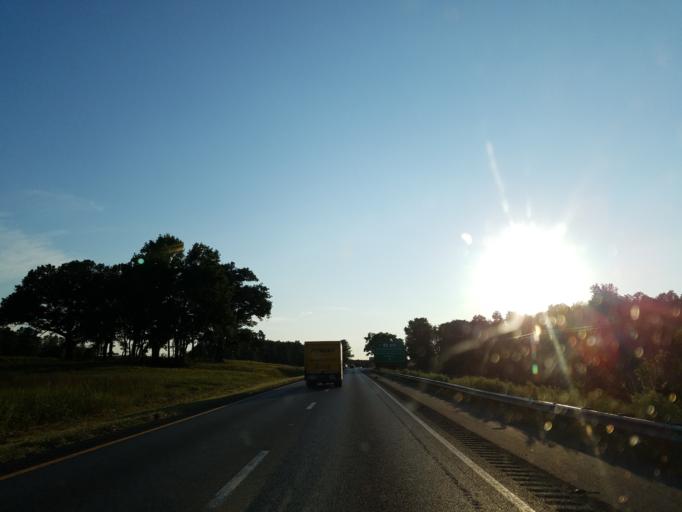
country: US
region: South Carolina
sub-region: Cherokee County
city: East Gaffney
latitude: 35.1043
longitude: -81.6198
